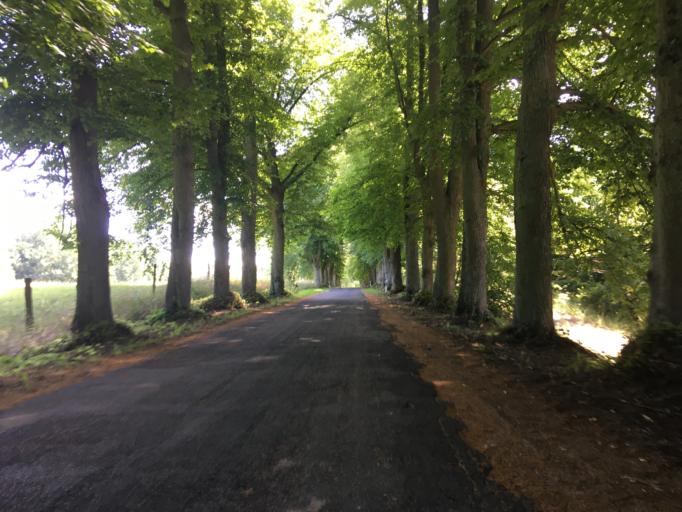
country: DE
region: Brandenburg
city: Templin
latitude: 53.1774
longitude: 13.5228
